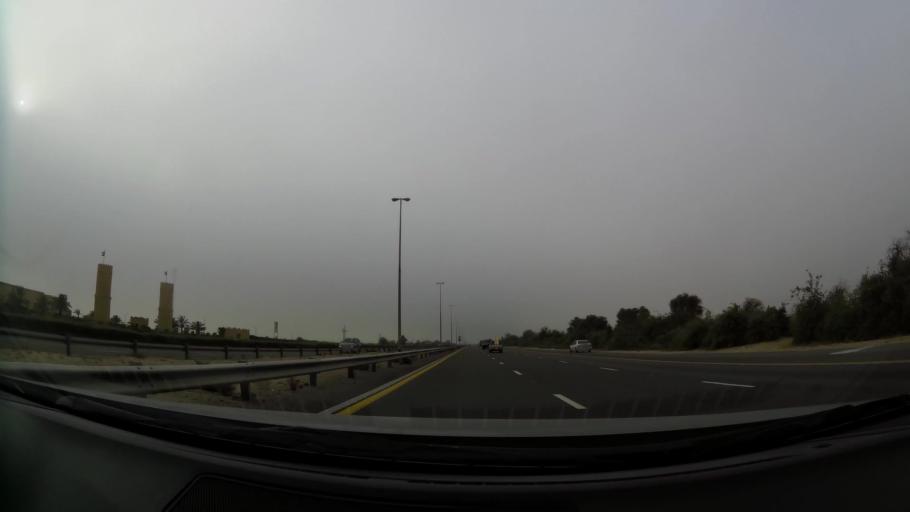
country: AE
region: Dubai
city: Dubai
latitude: 25.0699
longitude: 55.4068
